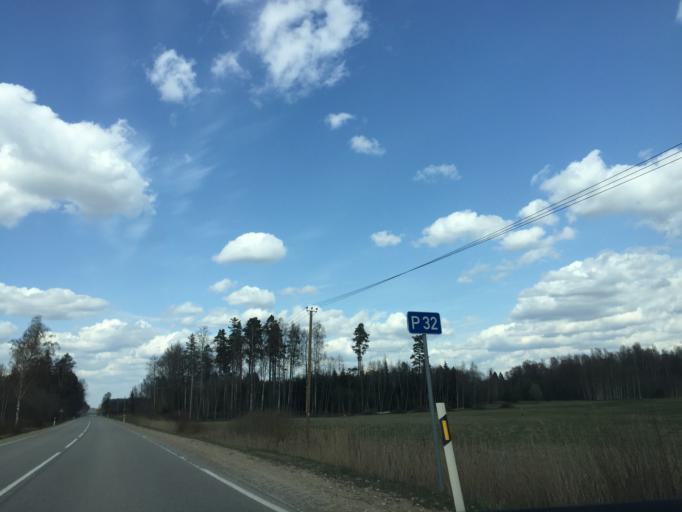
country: LV
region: Skriveri
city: Skriveri
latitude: 56.7606
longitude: 25.1705
